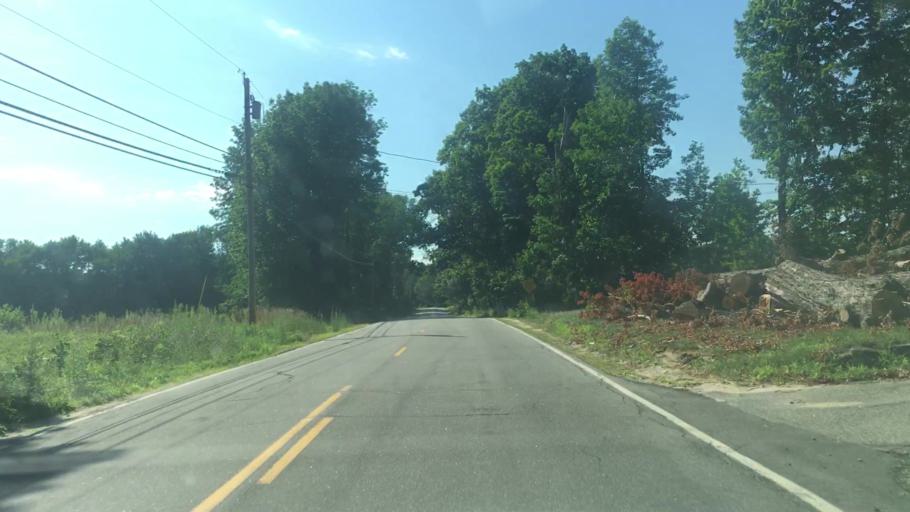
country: US
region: Maine
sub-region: York County
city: Hollis Center
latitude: 43.6321
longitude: -70.5650
